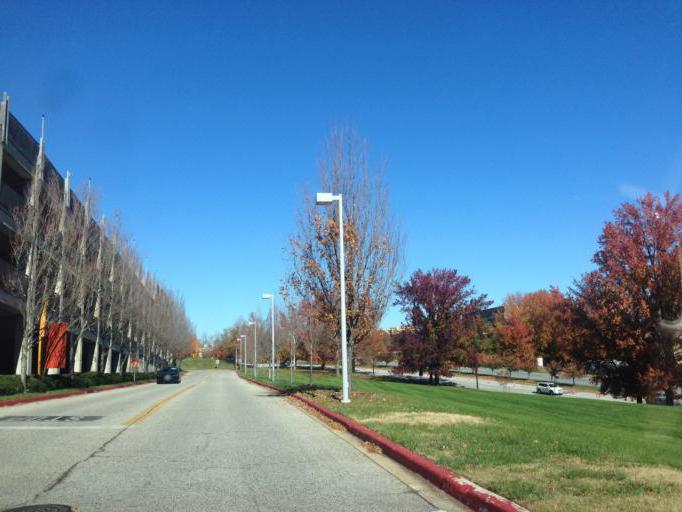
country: US
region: Maryland
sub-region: Howard County
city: Columbia
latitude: 39.2161
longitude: -76.8585
